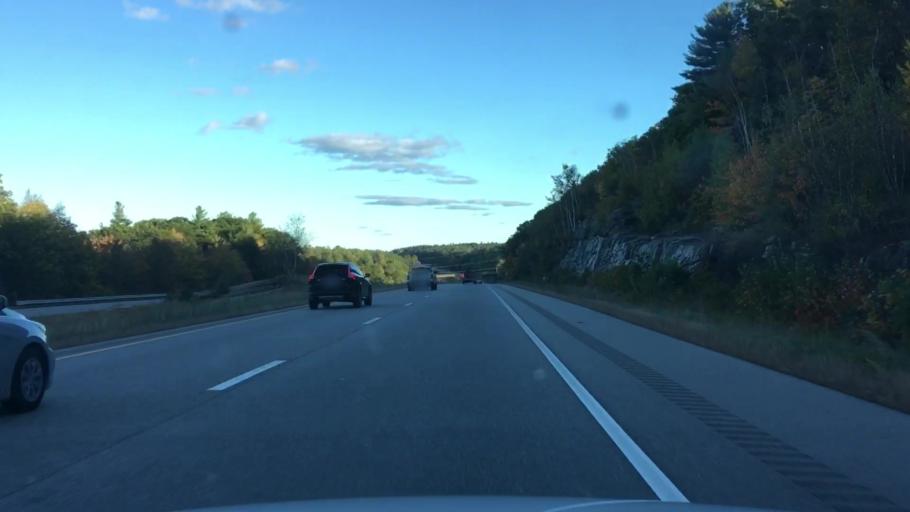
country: US
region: New Hampshire
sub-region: Rockingham County
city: Candia
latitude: 43.0390
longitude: -71.2626
